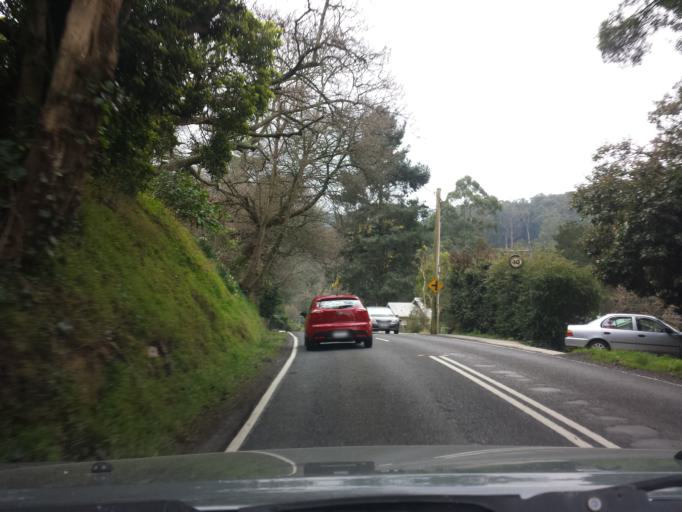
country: AU
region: Victoria
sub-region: Yarra Ranges
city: Belgrave
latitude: -37.9044
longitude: 145.3562
